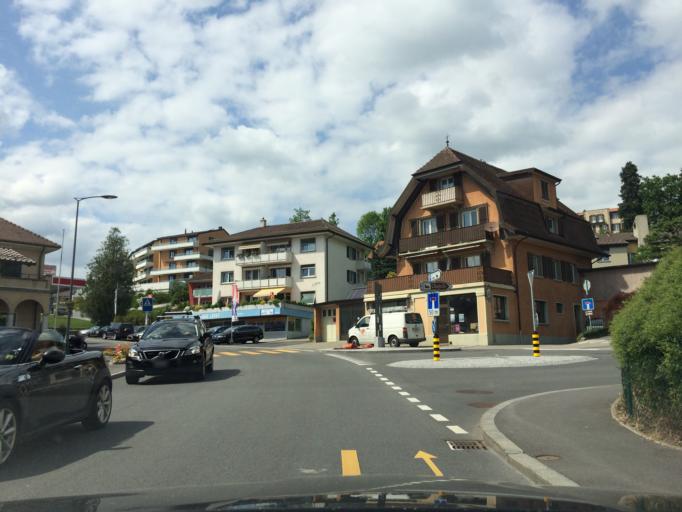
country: CH
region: Vaud
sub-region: Lavaux-Oron District
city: Chexbres
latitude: 46.4829
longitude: 6.7760
